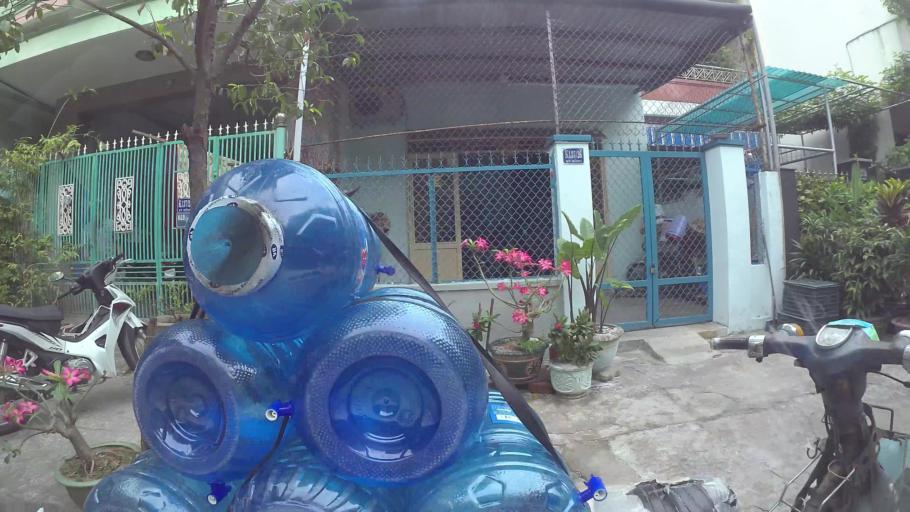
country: VN
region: Da Nang
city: Thanh Khe
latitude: 16.0694
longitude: 108.1861
